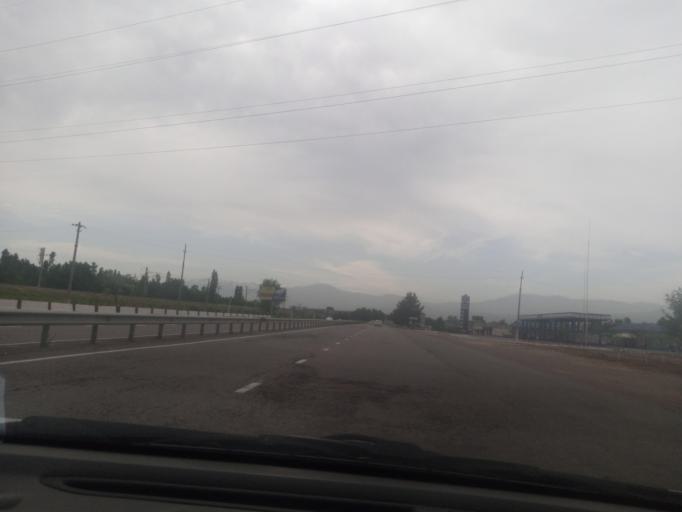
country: UZ
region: Toshkent
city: Ohangaron
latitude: 40.9088
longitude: 69.7917
